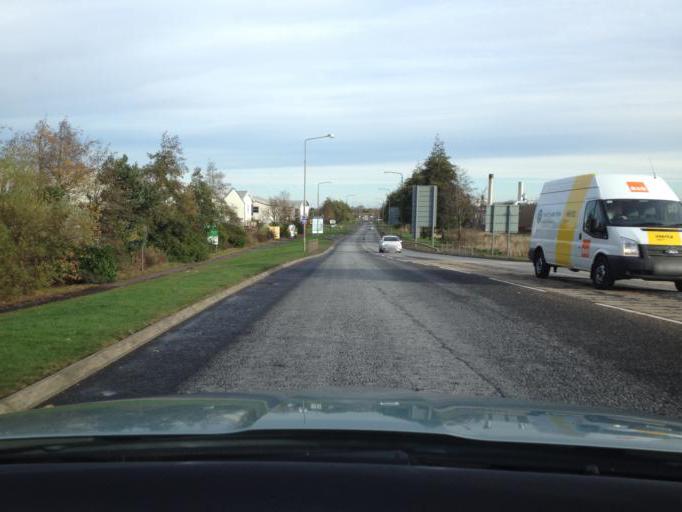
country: GB
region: Scotland
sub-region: West Lothian
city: Livingston
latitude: 55.9067
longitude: -3.5132
